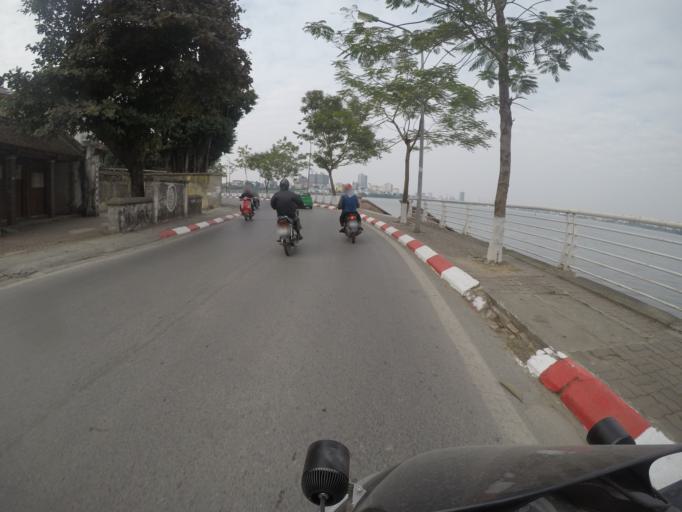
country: VN
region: Ha Noi
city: Tay Ho
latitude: 21.0552
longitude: 105.8117
